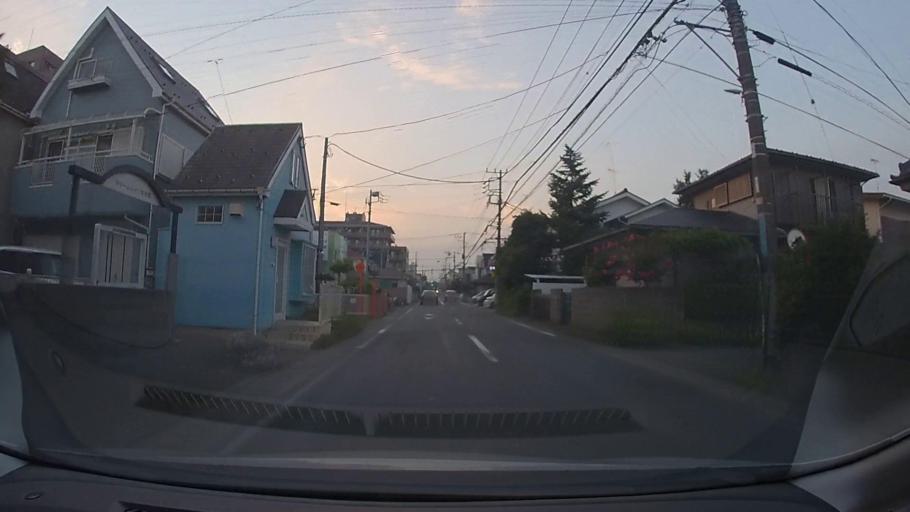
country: JP
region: Kanagawa
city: Minami-rinkan
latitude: 35.4953
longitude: 139.4438
